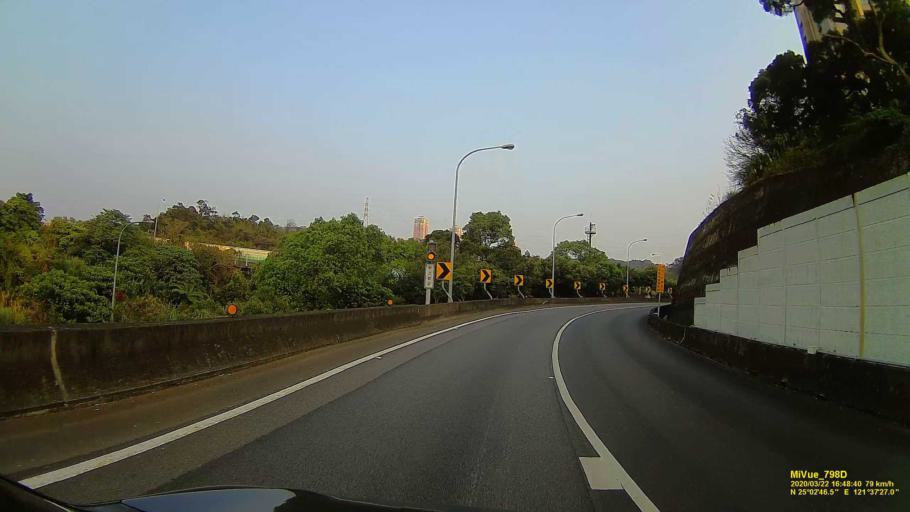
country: TW
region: Taipei
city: Taipei
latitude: 25.0459
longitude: 121.6245
